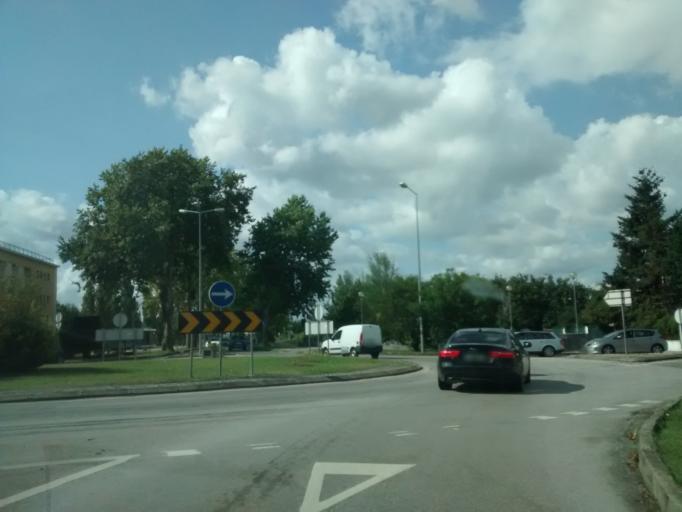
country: PT
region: Aveiro
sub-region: Mealhada
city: Mealhada
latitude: 40.3758
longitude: -8.4500
